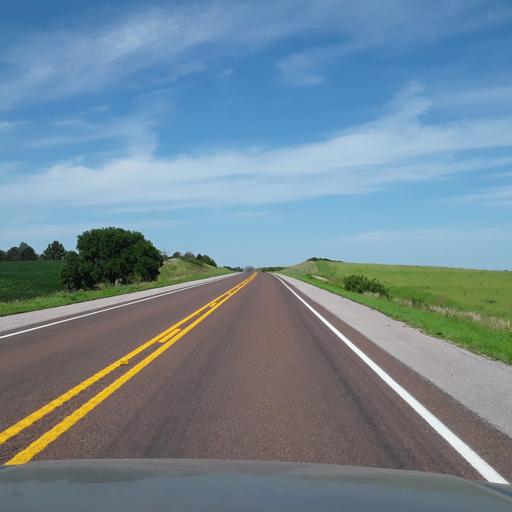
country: US
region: Nebraska
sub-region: Lancaster County
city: Lincoln
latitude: 40.8868
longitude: -96.8497
